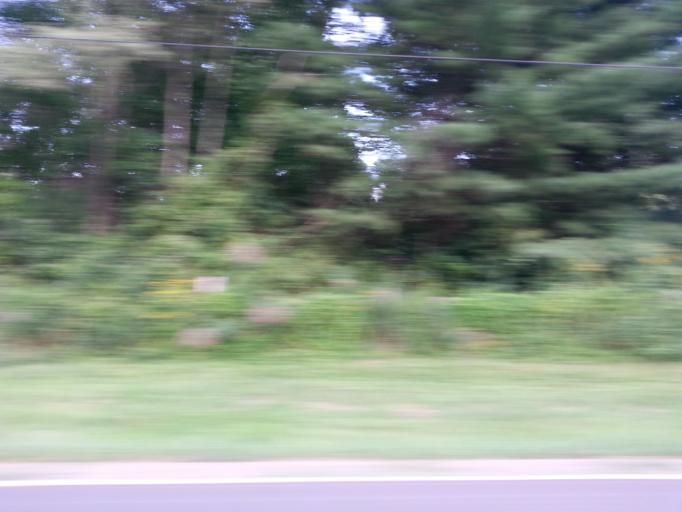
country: US
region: Tennessee
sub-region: Johnson County
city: Mountain City
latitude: 36.6082
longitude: -81.8099
